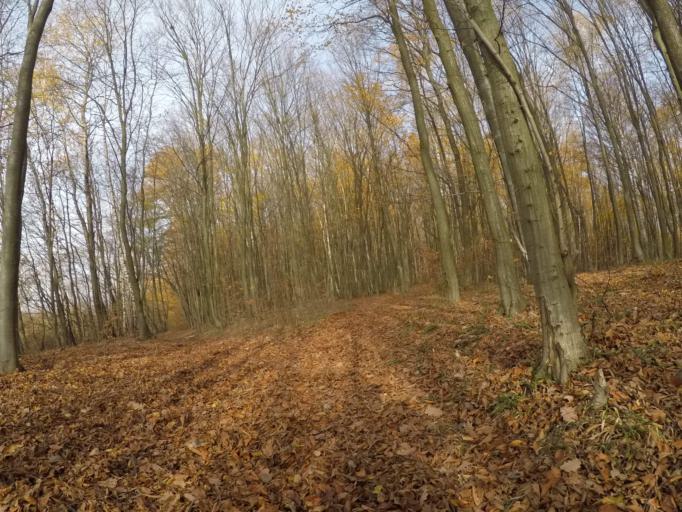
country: SK
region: Presovsky
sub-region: Okres Presov
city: Presov
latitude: 48.9239
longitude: 21.2203
